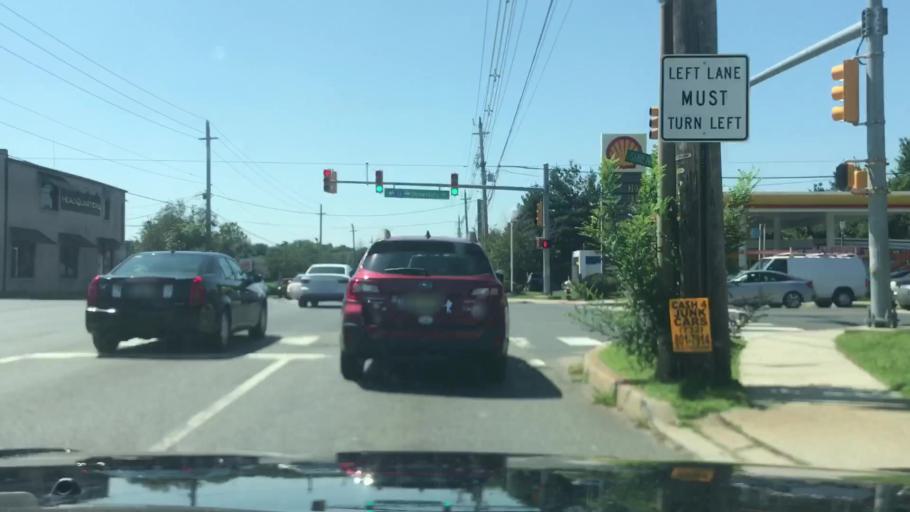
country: US
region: New Jersey
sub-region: Monmouth County
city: Red Bank
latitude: 40.3374
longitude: -74.0746
